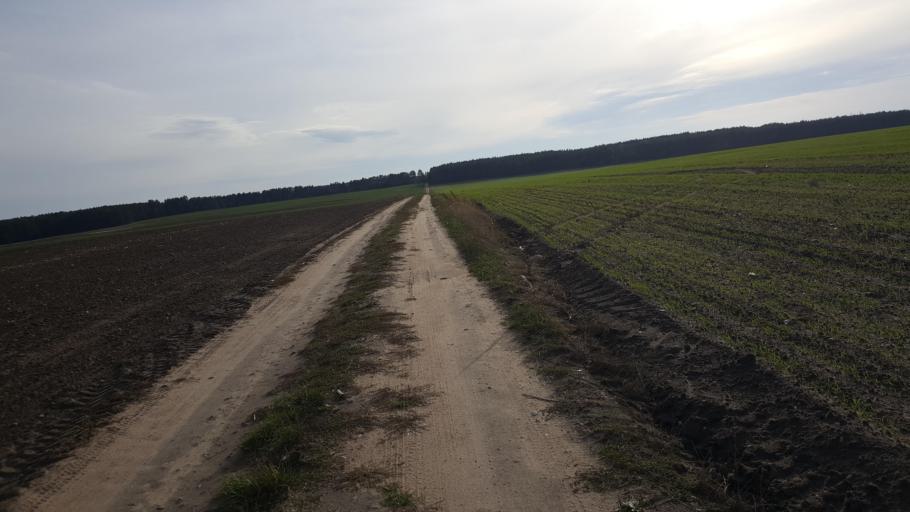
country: BY
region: Brest
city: Kamyanyets
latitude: 52.3959
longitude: 23.8535
